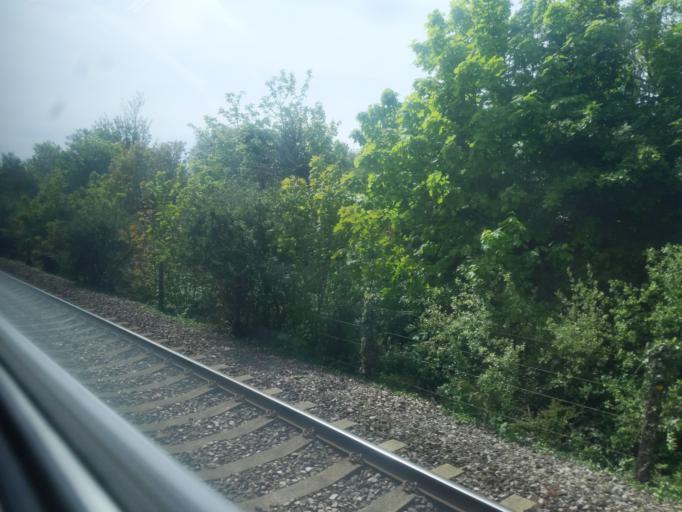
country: GB
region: England
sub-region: Cornwall
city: Hayle
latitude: 50.1688
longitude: -5.4468
